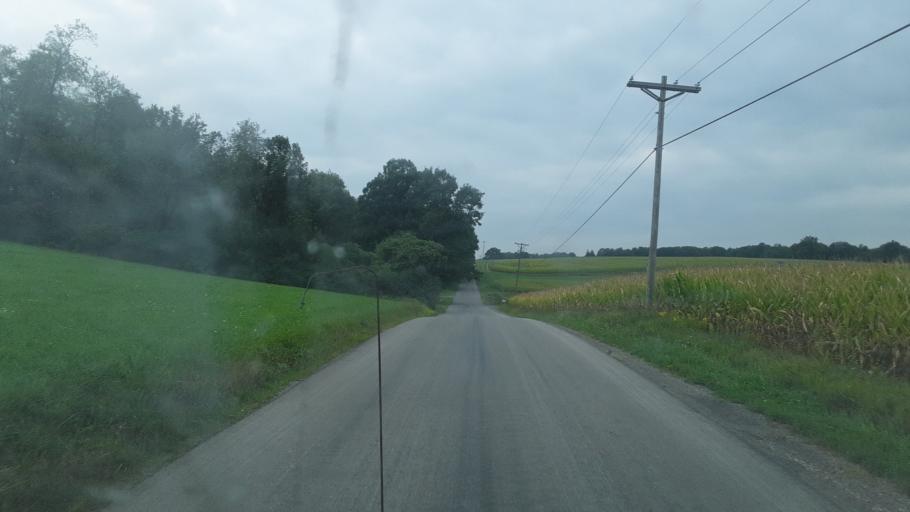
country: US
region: Pennsylvania
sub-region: Jefferson County
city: Punxsutawney
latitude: 40.9465
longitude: -79.1349
